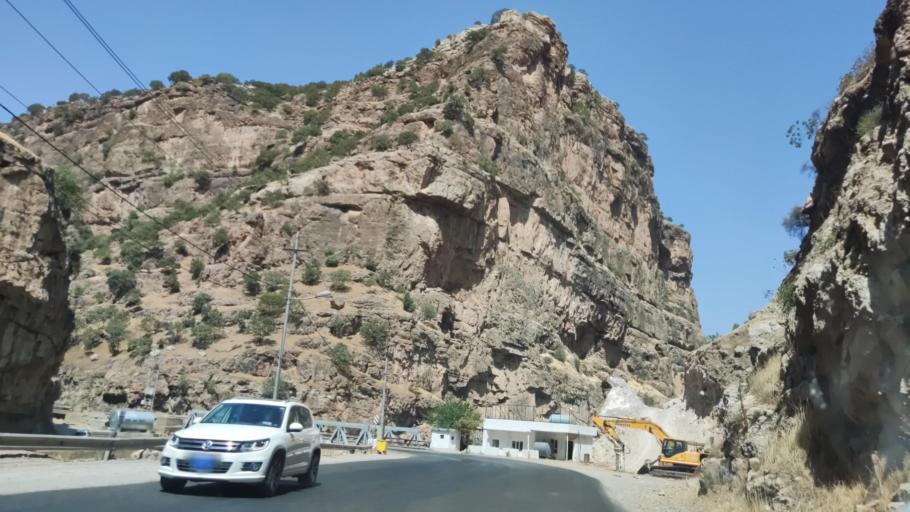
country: IQ
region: Arbil
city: Ruwandiz
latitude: 36.6294
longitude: 44.4577
